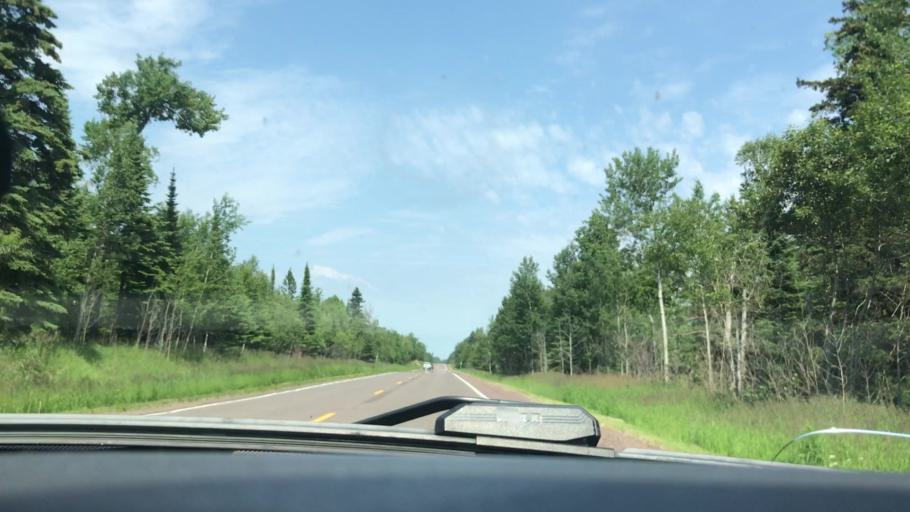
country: US
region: Minnesota
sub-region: Lake County
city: Silver Bay
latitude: 47.5034
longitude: -90.9623
